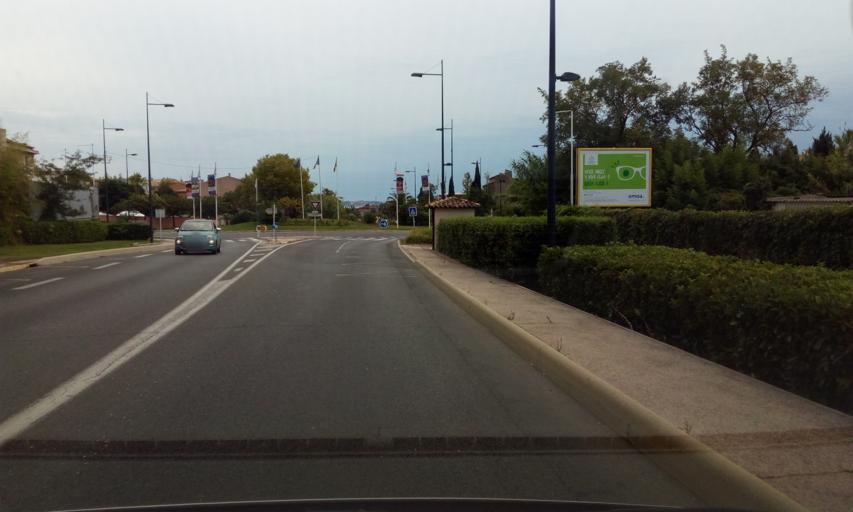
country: FR
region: Provence-Alpes-Cote d'Azur
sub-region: Departement du Var
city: Carqueiranne
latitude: 43.0965
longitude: 6.0688
